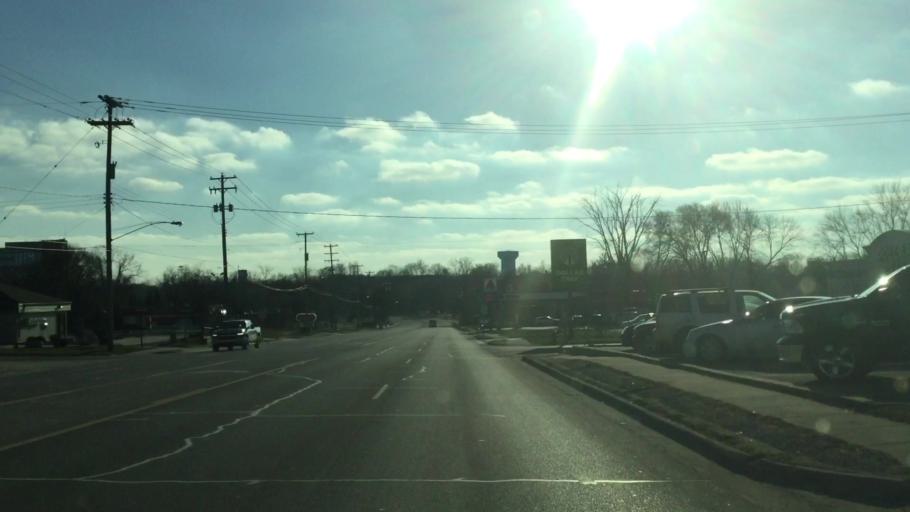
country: US
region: Michigan
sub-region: Genesee County
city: Flint
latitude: 43.0219
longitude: -83.7332
